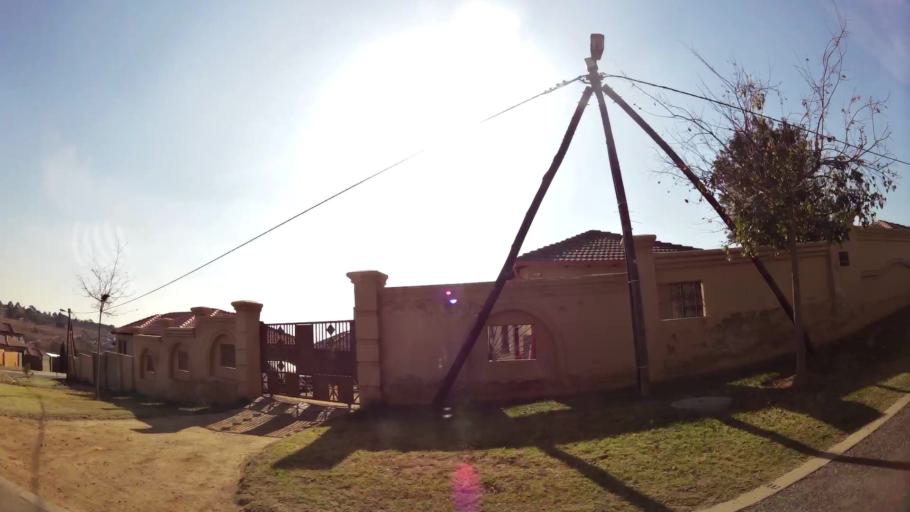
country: ZA
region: Gauteng
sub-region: West Rand District Municipality
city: Muldersdriseloop
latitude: -26.0451
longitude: 27.9202
